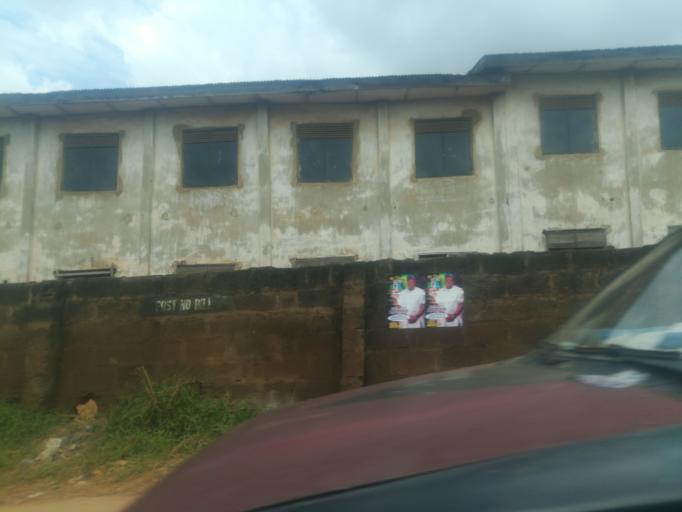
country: NG
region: Oyo
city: Ibadan
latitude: 7.4131
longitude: 3.9333
